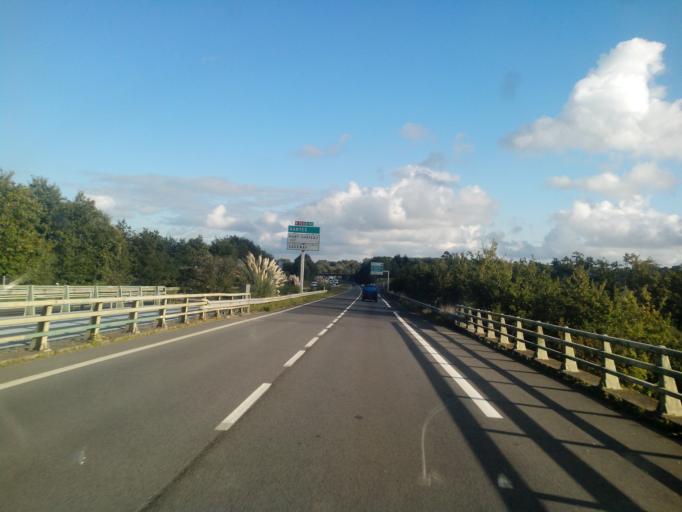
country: FR
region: Pays de la Loire
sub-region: Departement de la Loire-Atlantique
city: Pontchateau
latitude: 47.4410
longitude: -2.0785
